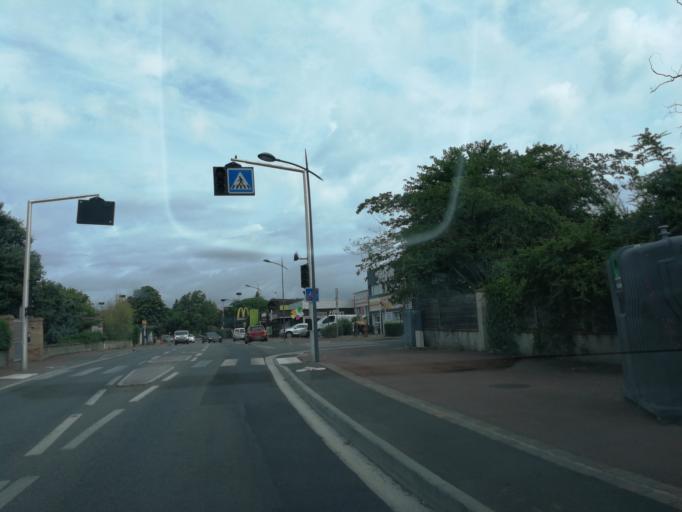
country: FR
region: Midi-Pyrenees
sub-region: Departement de la Haute-Garonne
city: Aucamville
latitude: 43.6603
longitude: 1.4317
